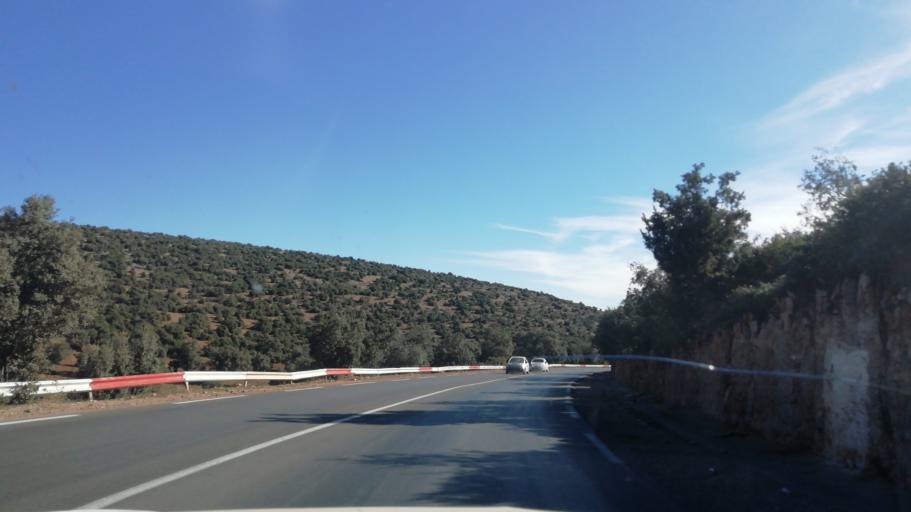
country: DZ
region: Tlemcen
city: Sebdou
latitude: 34.7394
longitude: -1.3387
